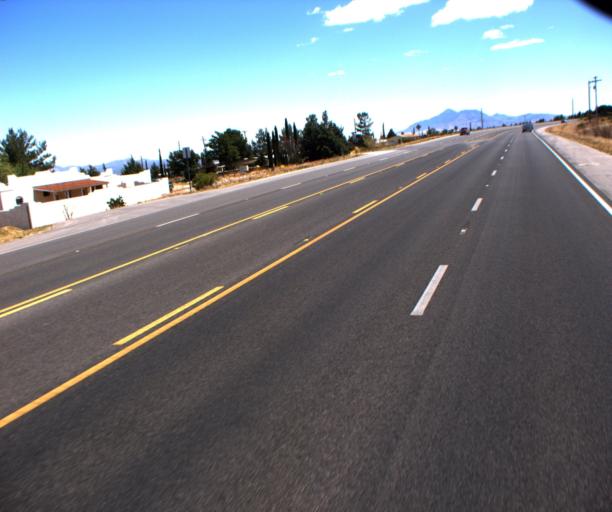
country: US
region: Arizona
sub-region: Cochise County
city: Sierra Vista Southeast
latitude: 31.4348
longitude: -110.2446
